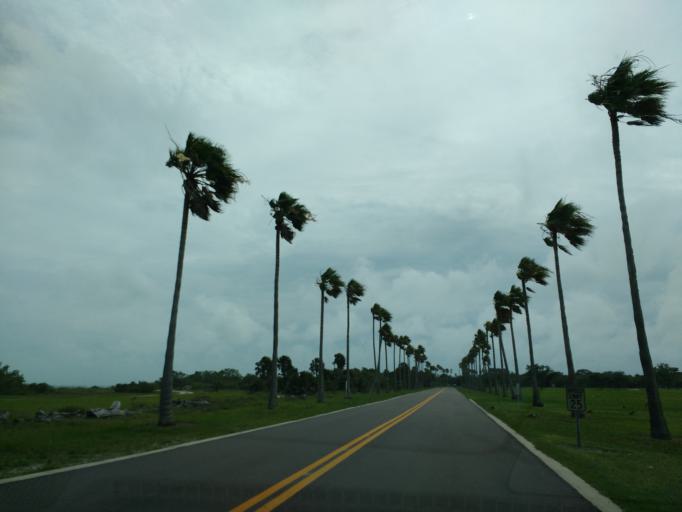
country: US
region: Florida
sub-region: Pinellas County
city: Tierra Verde
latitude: 27.6153
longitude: -82.7302
